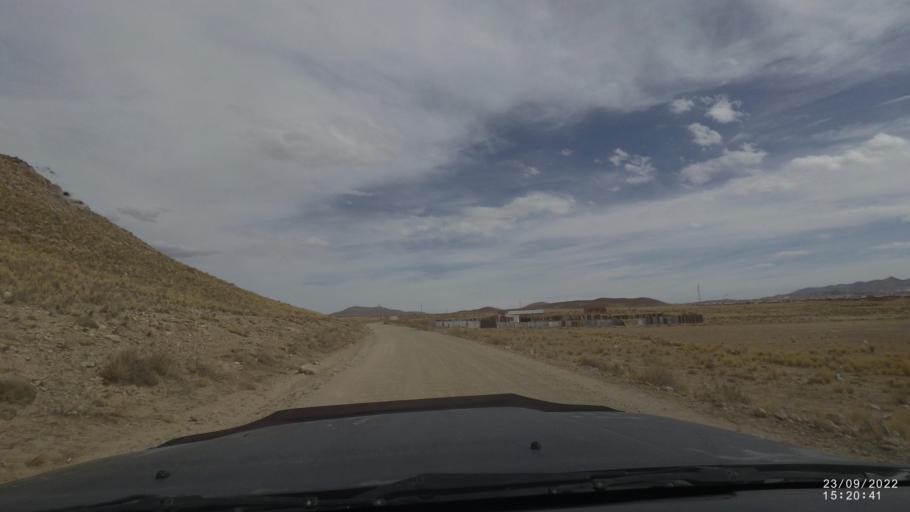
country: BO
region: Oruro
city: Oruro
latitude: -17.8989
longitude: -67.0453
